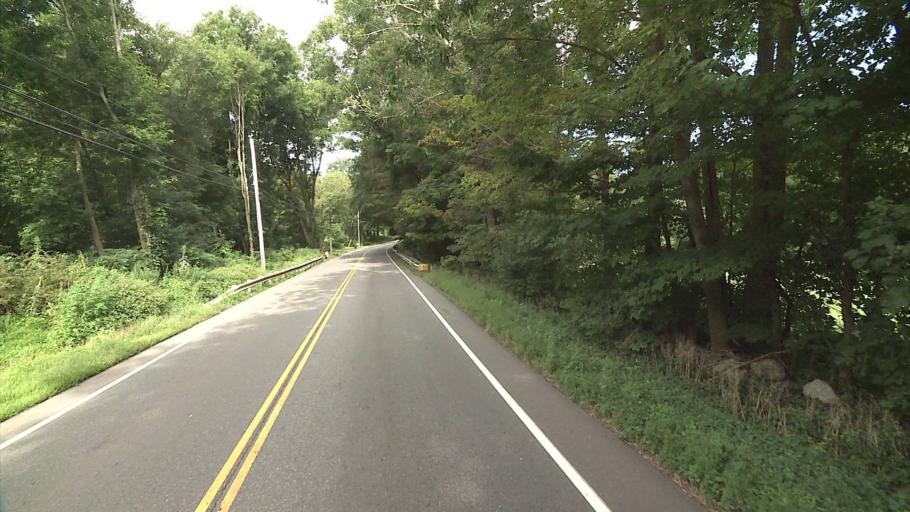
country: US
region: Connecticut
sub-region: New London County
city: Baltic
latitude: 41.6087
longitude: -72.1417
